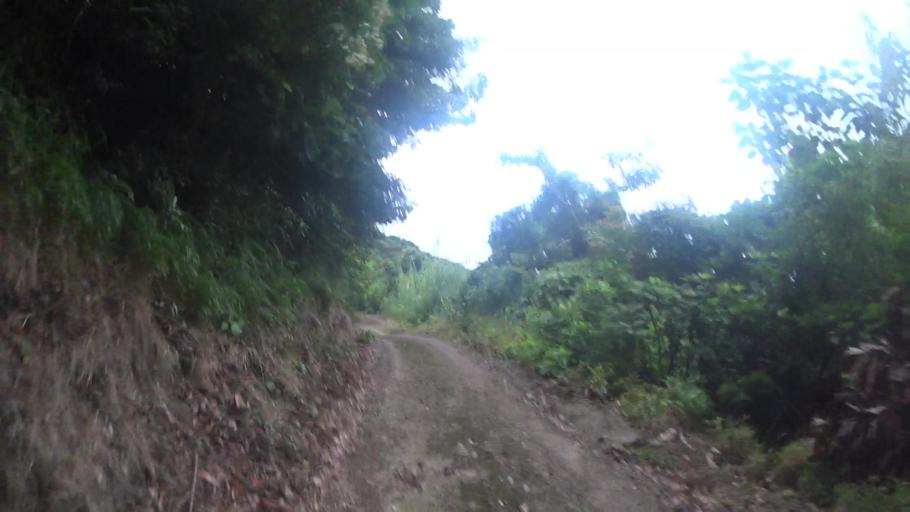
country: JP
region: Nagasaki
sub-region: Hirado Shi
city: Hirado
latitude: 33.1829
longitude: 129.3562
